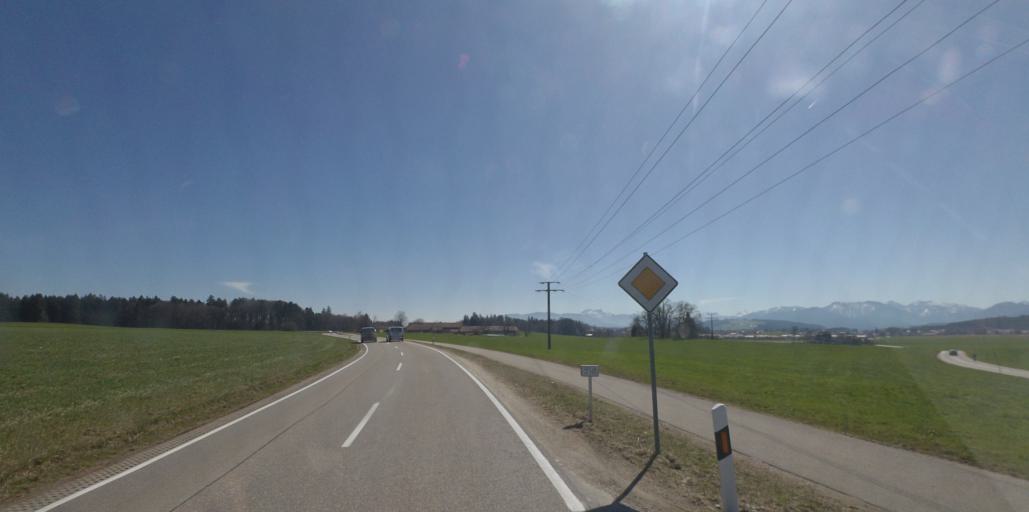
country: DE
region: Bavaria
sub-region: Upper Bavaria
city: Nussdorf
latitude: 47.8876
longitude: 12.6161
